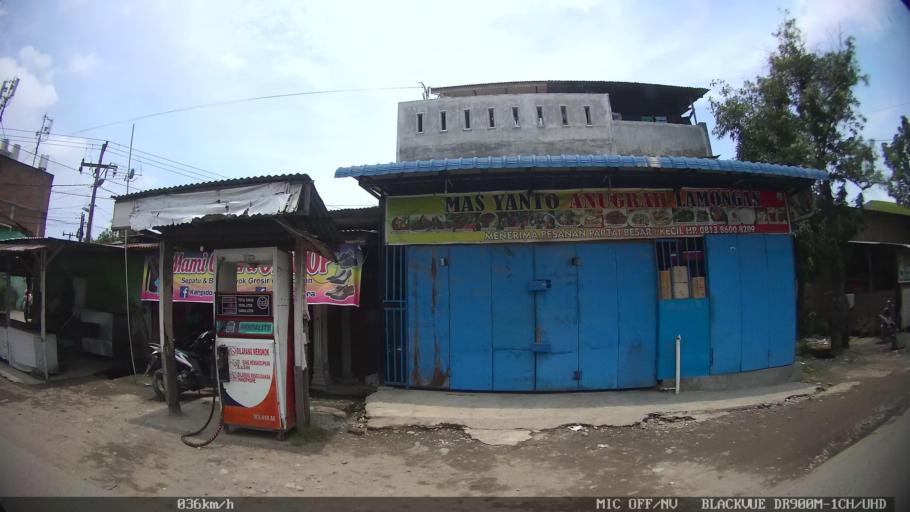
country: ID
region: North Sumatra
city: Labuhan Deli
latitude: 3.6784
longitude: 98.6717
